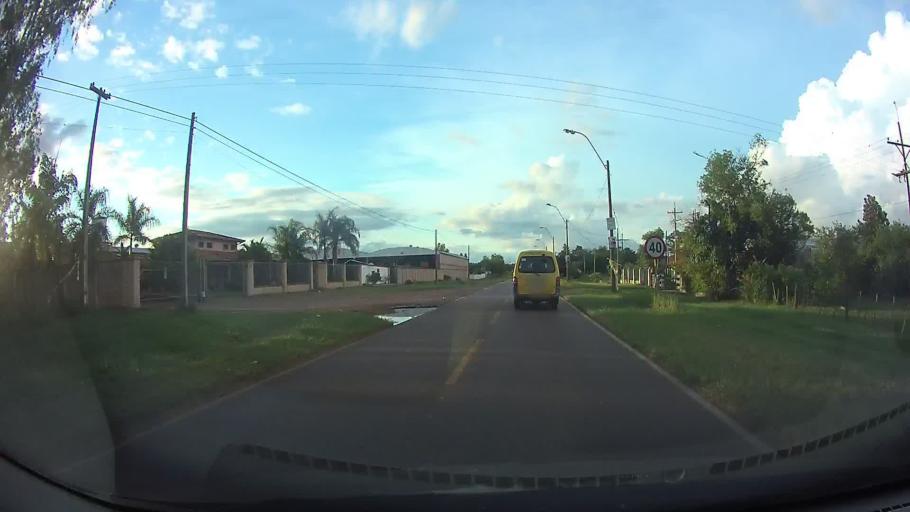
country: PY
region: Paraguari
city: Carapegua
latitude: -25.7743
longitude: -57.2301
